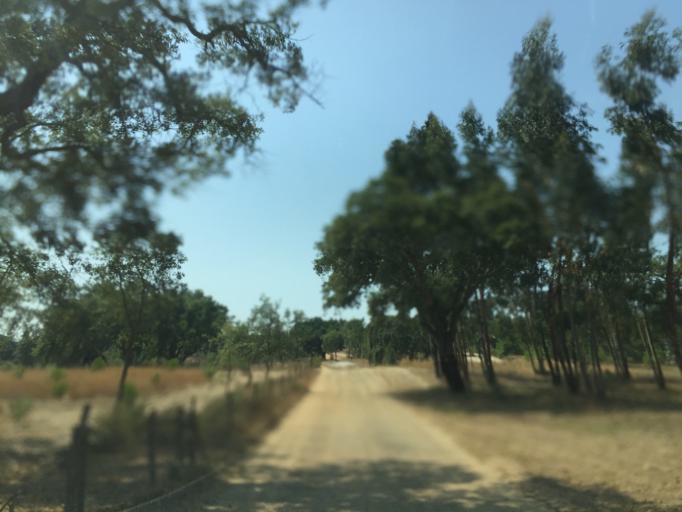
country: PT
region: Setubal
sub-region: Grandola
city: Grandola
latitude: 38.0037
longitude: -8.4896
